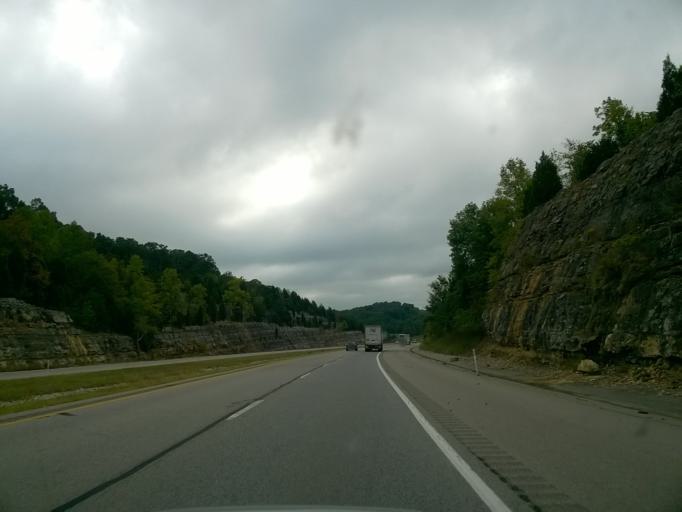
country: US
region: Indiana
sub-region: Harrison County
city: Corydon
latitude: 38.2384
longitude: -86.2459
